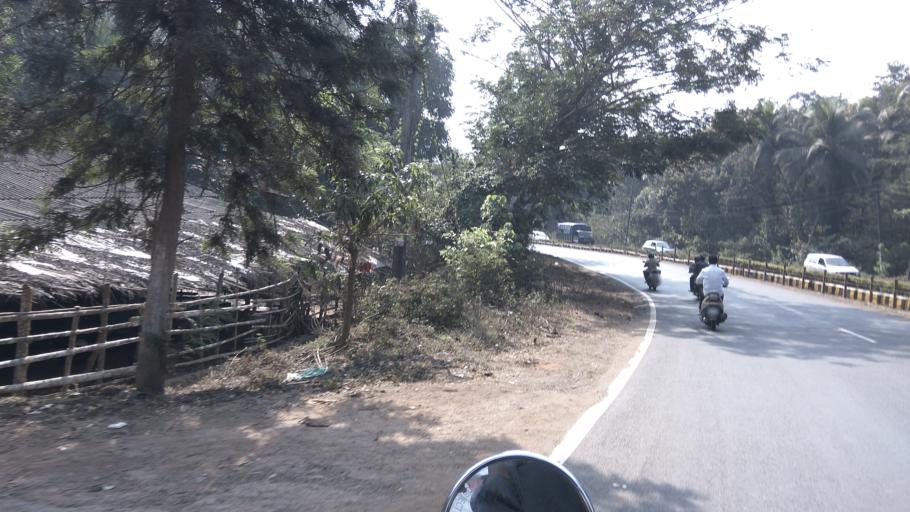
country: IN
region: Goa
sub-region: North Goa
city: Bandora
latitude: 15.4519
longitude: 73.9658
